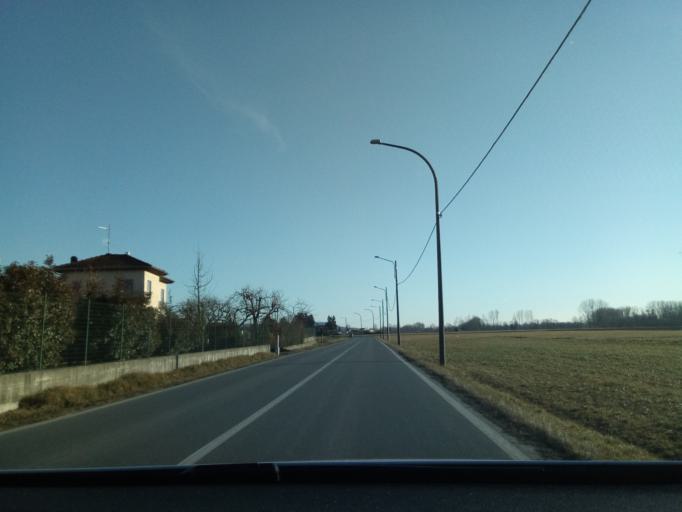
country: IT
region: Piedmont
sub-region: Provincia di Torino
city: Cascinette d'Ivrea
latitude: 45.4574
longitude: 7.9078
